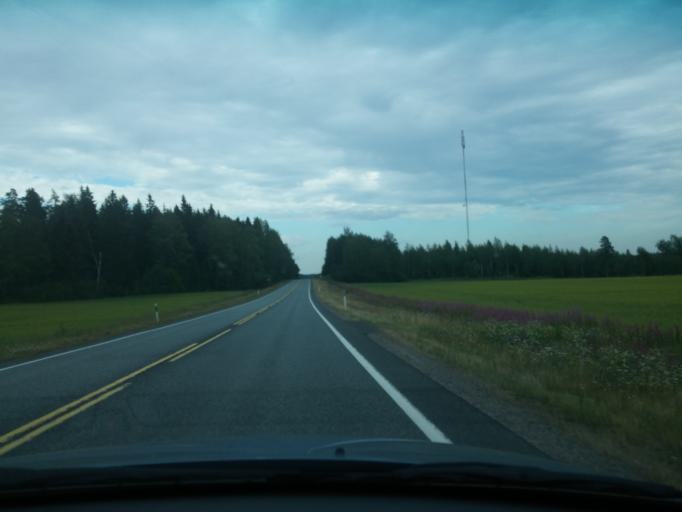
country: FI
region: Haeme
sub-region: Haemeenlinna
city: Tervakoski
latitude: 60.7393
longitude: 24.5901
